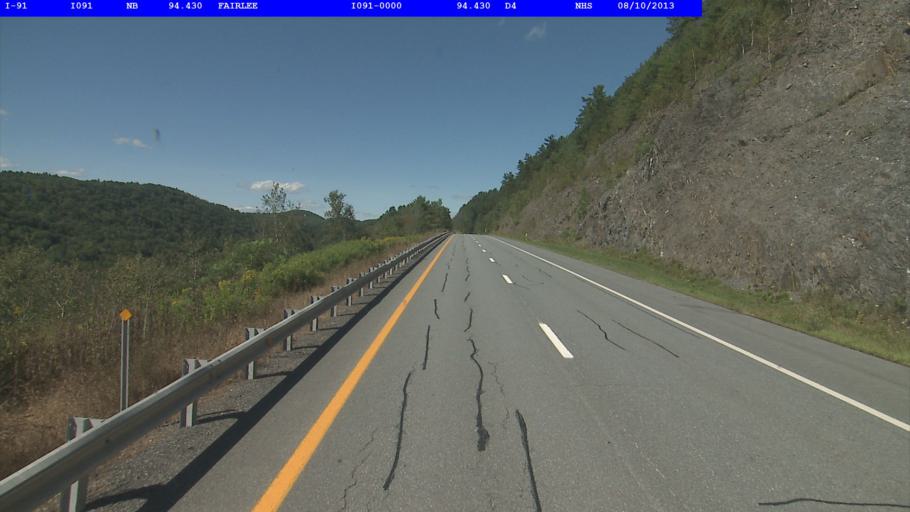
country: US
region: New Hampshire
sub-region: Grafton County
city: Orford
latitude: 43.9393
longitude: -72.1326
